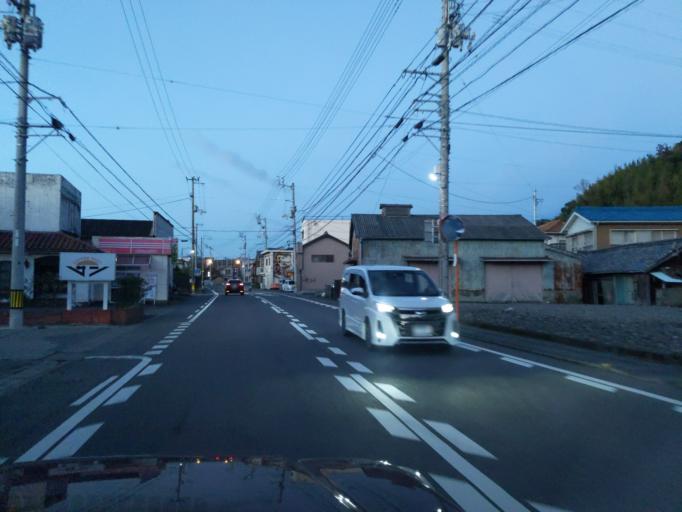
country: JP
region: Tokushima
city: Anan
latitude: 33.8759
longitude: 134.6455
